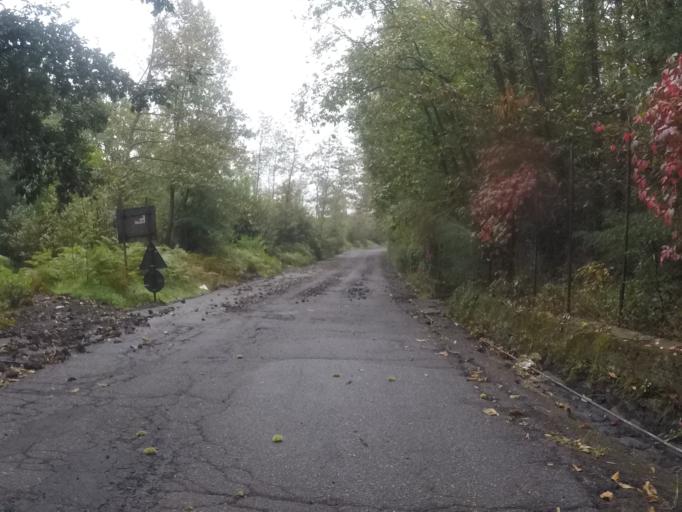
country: IT
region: Sicily
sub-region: Catania
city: Pedara
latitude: 37.6616
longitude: 15.0392
